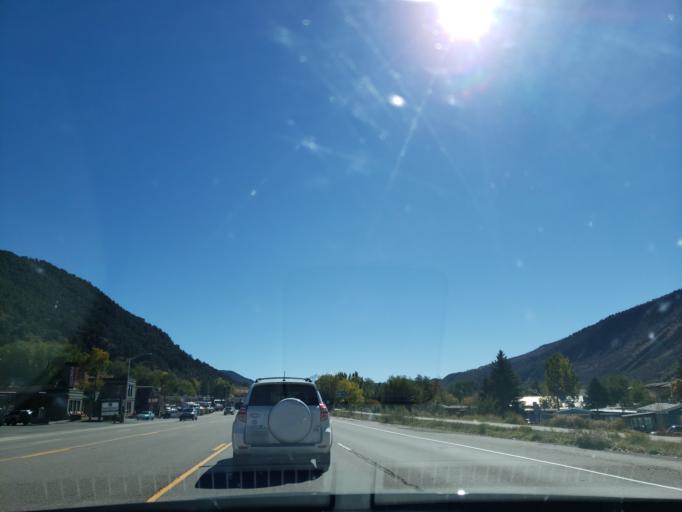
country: US
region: Colorado
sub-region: Garfield County
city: Glenwood Springs
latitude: 39.5284
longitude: -107.3244
